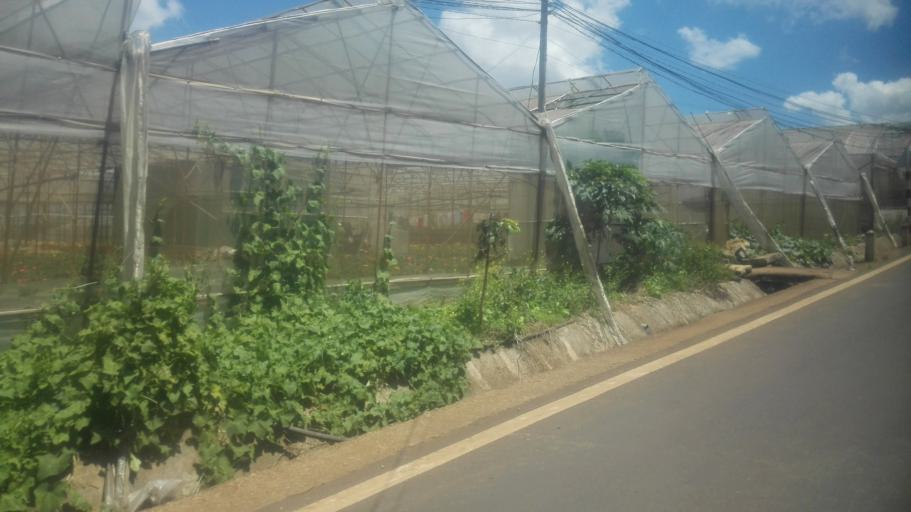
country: VN
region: Lam Dong
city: Da Lat
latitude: 11.9284
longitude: 108.3505
